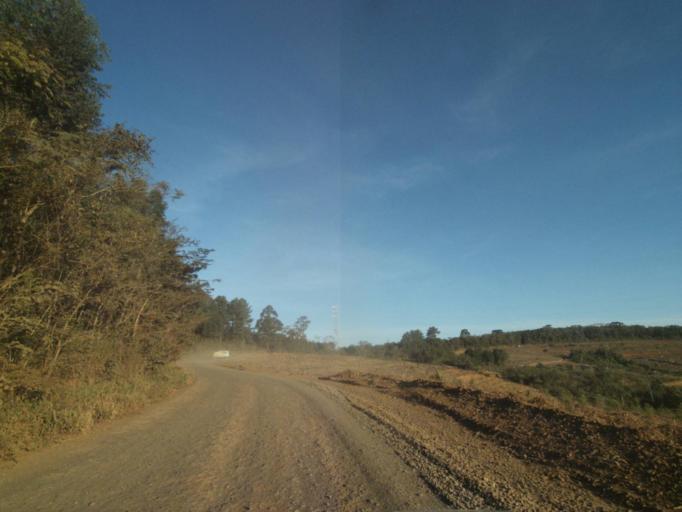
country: BR
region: Parana
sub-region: Telemaco Borba
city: Telemaco Borba
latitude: -24.4206
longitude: -50.5899
